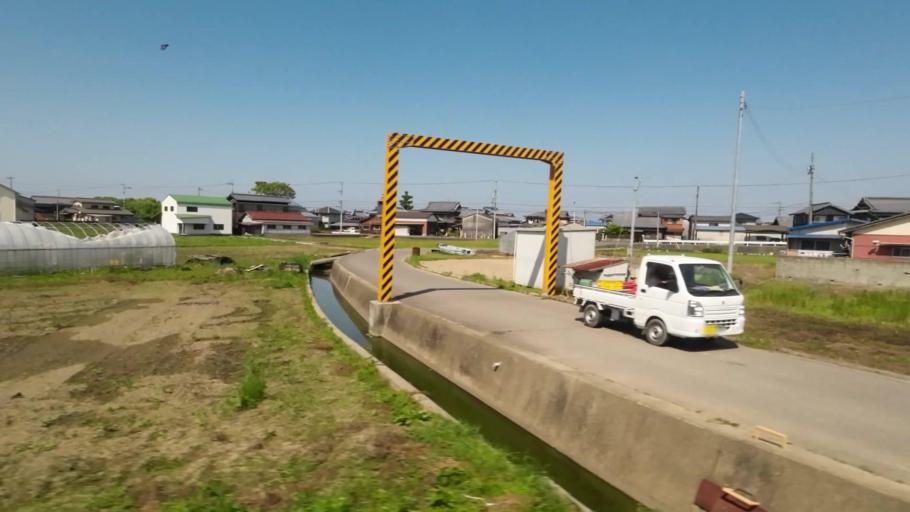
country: JP
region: Kagawa
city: Kan'onjicho
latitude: 34.1074
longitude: 133.6500
